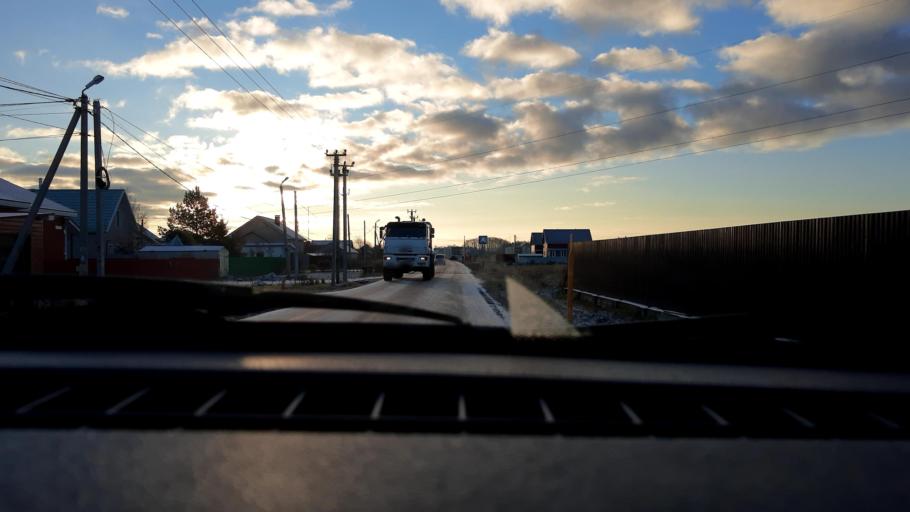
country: RU
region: Bashkortostan
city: Mikhaylovka
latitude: 54.7887
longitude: 55.8264
